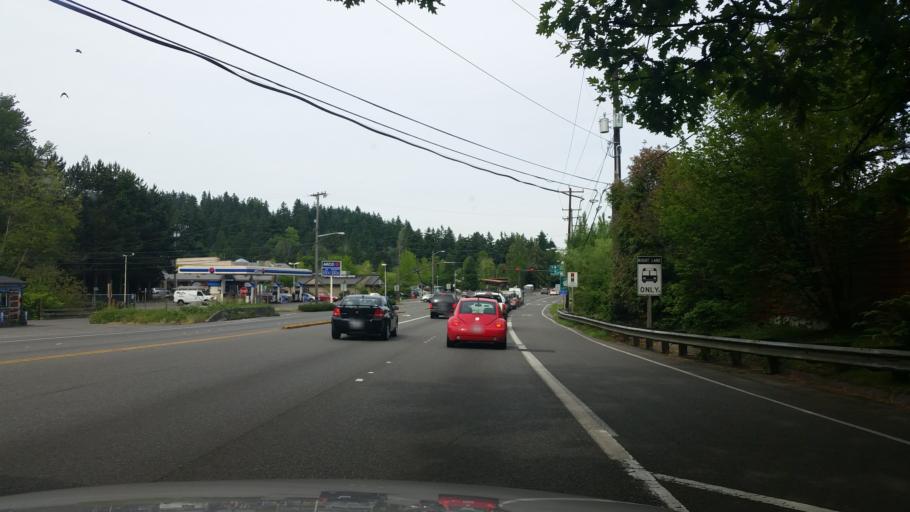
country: US
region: Washington
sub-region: King County
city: Lake Forest Park
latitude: 47.7512
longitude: -122.2817
